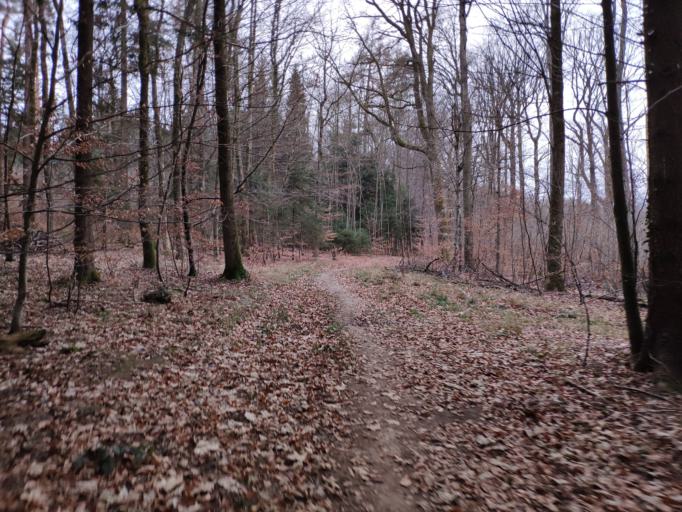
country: DE
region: Baden-Wuerttemberg
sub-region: Freiburg Region
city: Inzlingen
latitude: 47.5999
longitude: 7.6920
